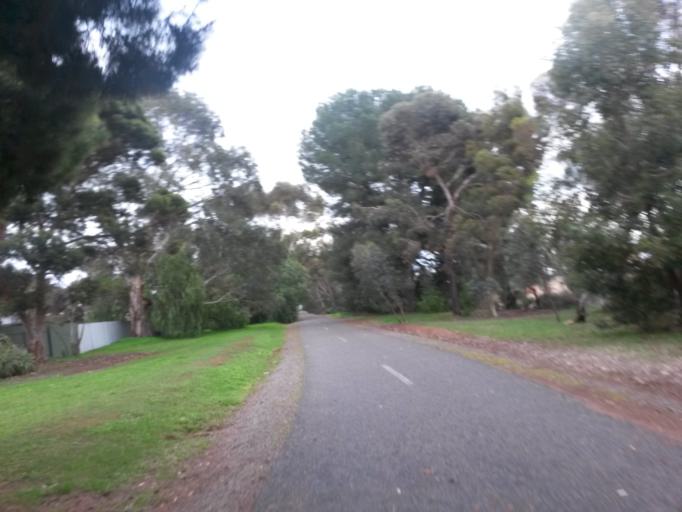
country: AU
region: South Australia
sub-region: Onkaparinga
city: McLaren Vale
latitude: -35.2136
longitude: 138.5330
